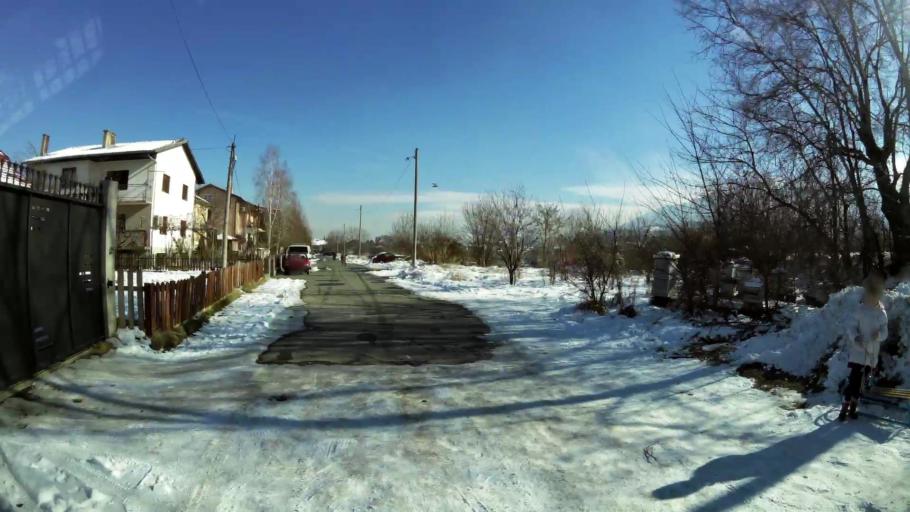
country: MK
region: Saraj
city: Saraj
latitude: 42.0038
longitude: 21.3471
